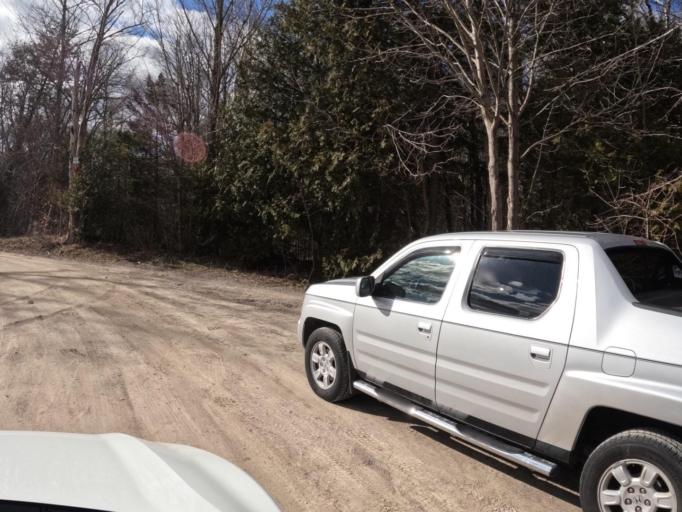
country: CA
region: Ontario
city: Norfolk County
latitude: 42.7655
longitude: -80.2948
